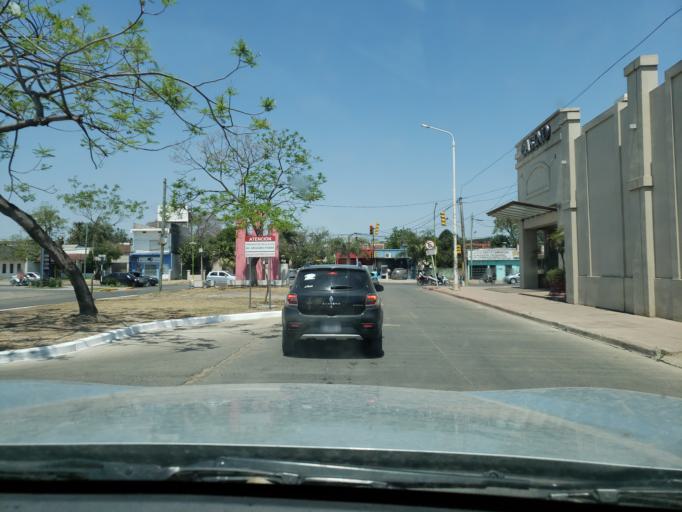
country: AR
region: Corrientes
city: Corrientes
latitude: -27.4722
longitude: -58.8062
